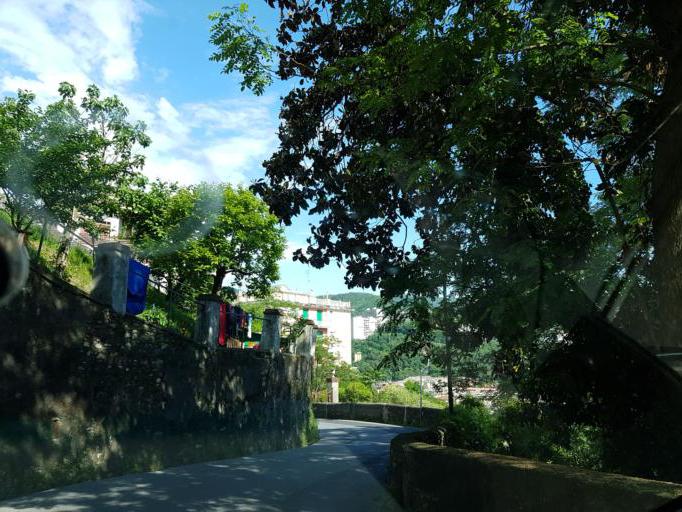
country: IT
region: Liguria
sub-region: Provincia di Genova
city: Manesseno
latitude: 44.4589
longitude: 8.8951
